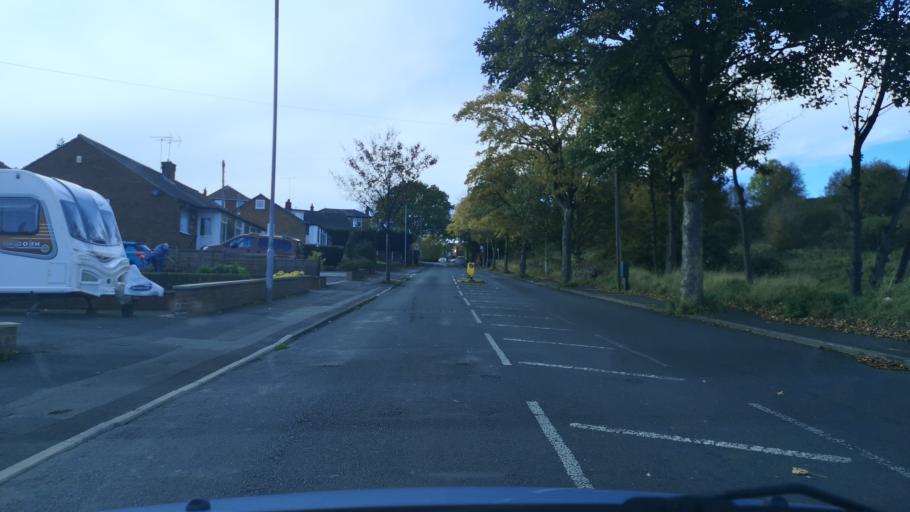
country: GB
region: England
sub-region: Kirklees
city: Heckmondwike
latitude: 53.7209
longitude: -1.6619
